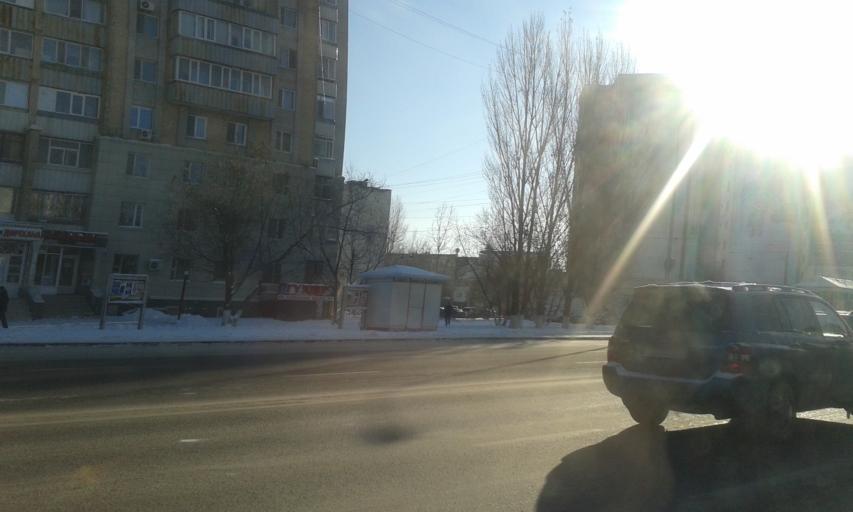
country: KZ
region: Astana Qalasy
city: Astana
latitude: 51.1577
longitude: 71.4365
